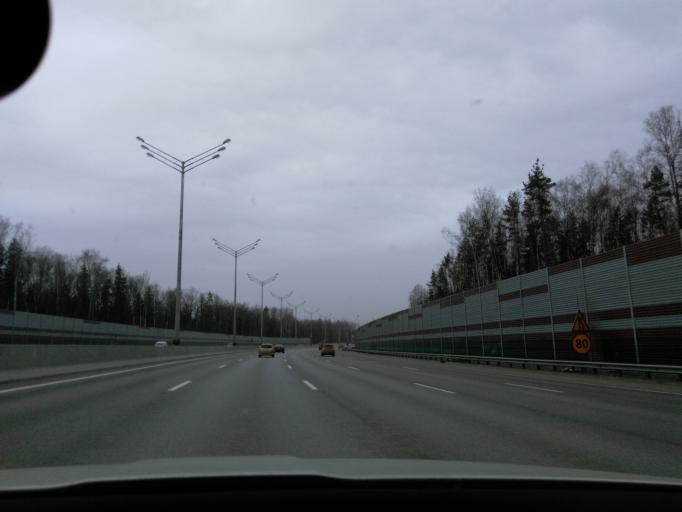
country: RU
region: Moscow
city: Khimki
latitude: 55.9439
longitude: 37.4467
